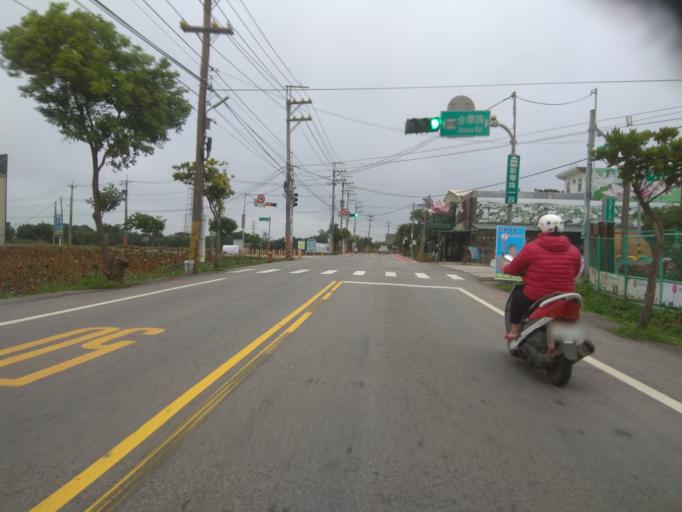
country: TW
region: Taiwan
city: Taoyuan City
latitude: 24.9993
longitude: 121.1217
